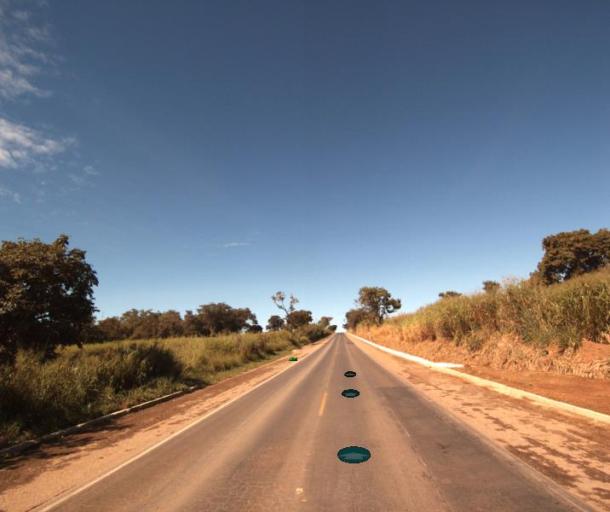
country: BR
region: Goias
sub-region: Itapaci
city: Itapaci
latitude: -14.8845
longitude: -49.3391
